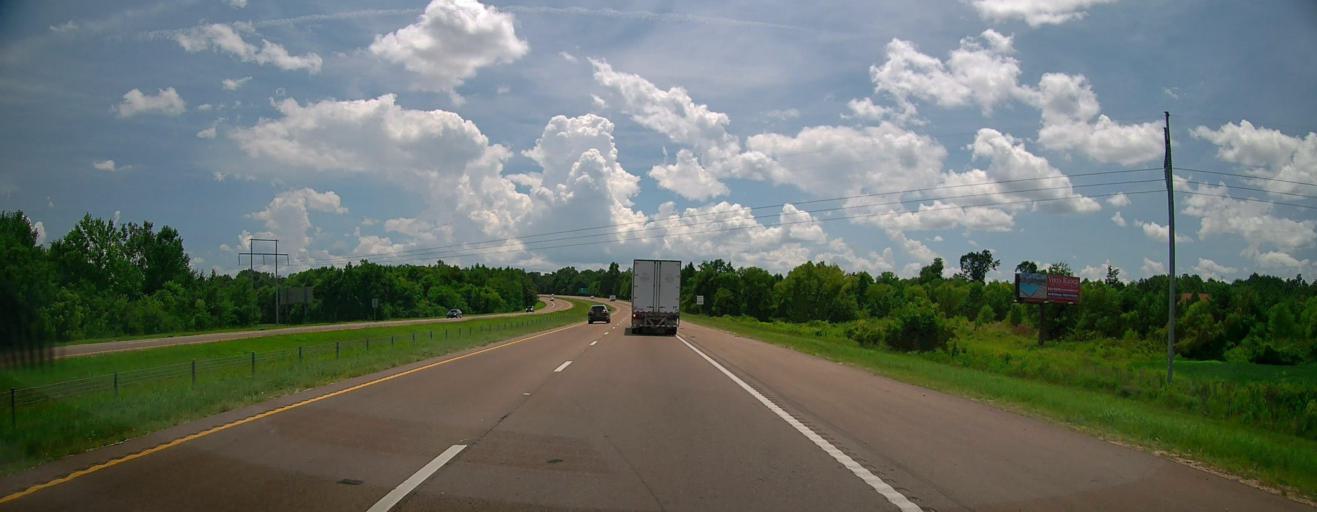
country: US
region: Mississippi
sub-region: Lee County
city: Tupelo
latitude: 34.2884
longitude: -88.7061
